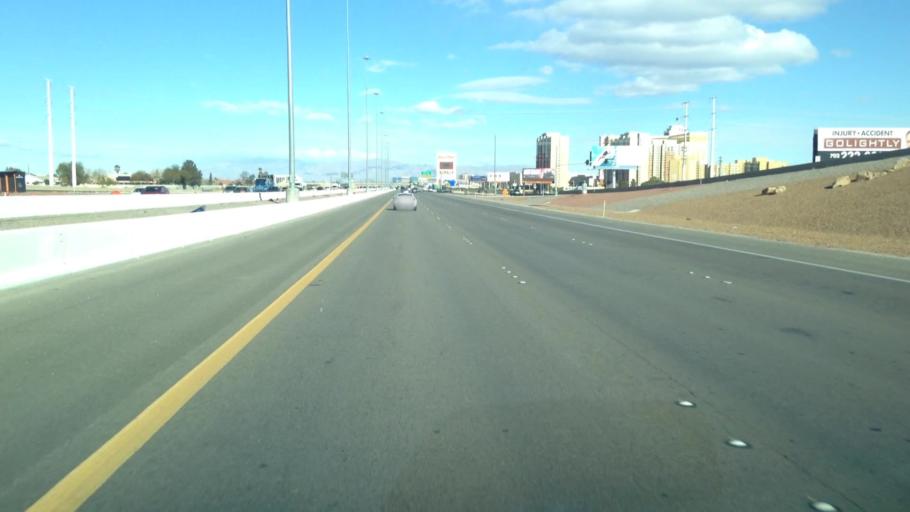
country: US
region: Nevada
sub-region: Clark County
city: Enterprise
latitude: 35.9998
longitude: -115.1805
